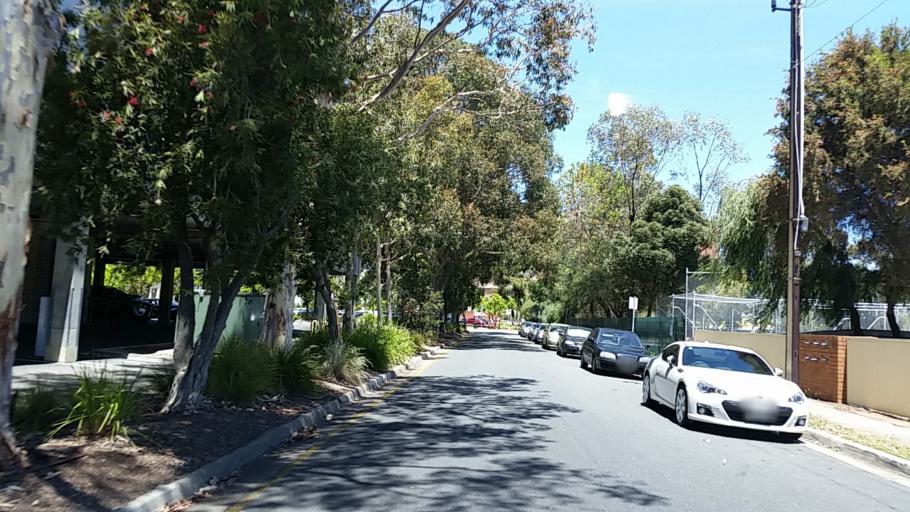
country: AU
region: South Australia
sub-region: Charles Sturt
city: Woodville West
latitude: -34.8812
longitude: 138.5337
